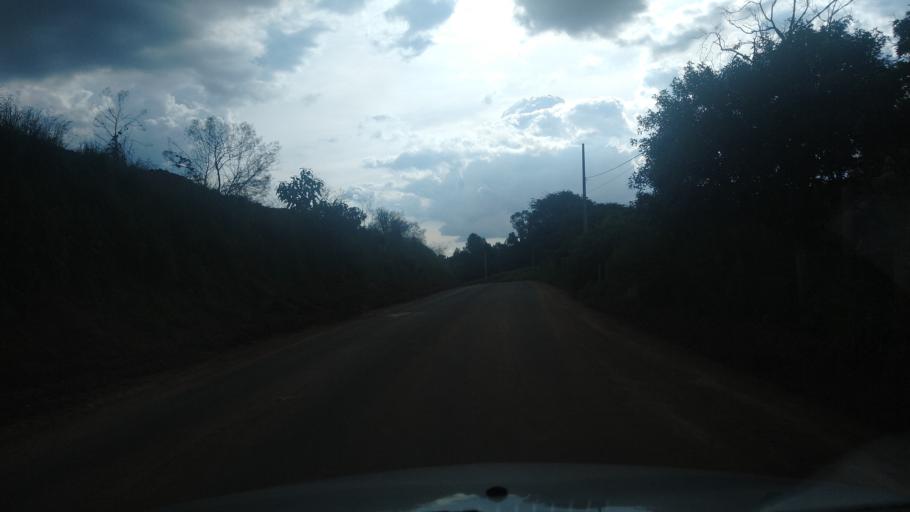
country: BR
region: Minas Gerais
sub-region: Extrema
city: Extrema
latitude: -22.7251
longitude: -46.3503
